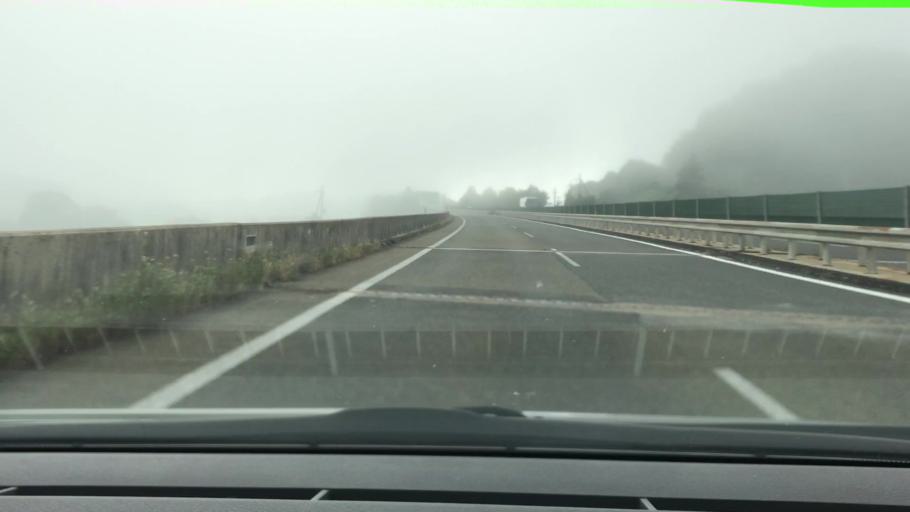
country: JP
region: Hyogo
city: Sasayama
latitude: 35.0712
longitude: 135.1740
